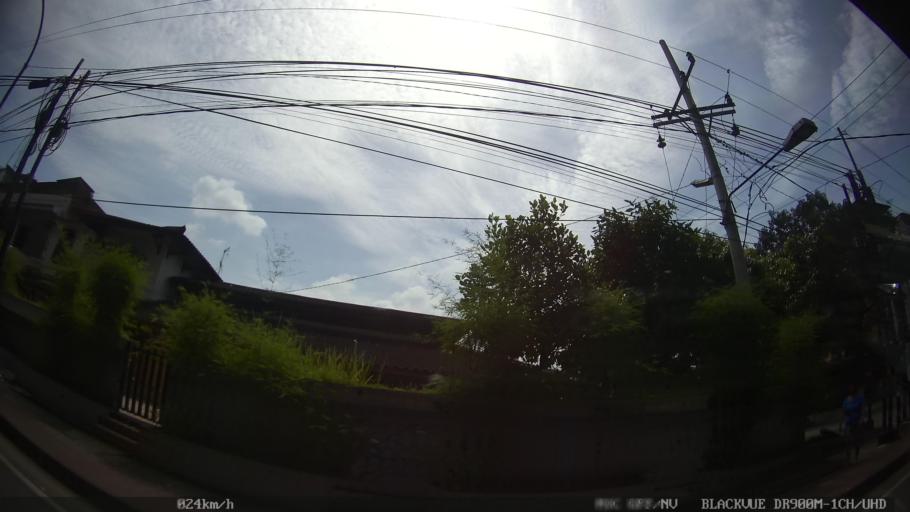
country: ID
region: North Sumatra
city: Medan
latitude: 3.5896
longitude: 98.6584
